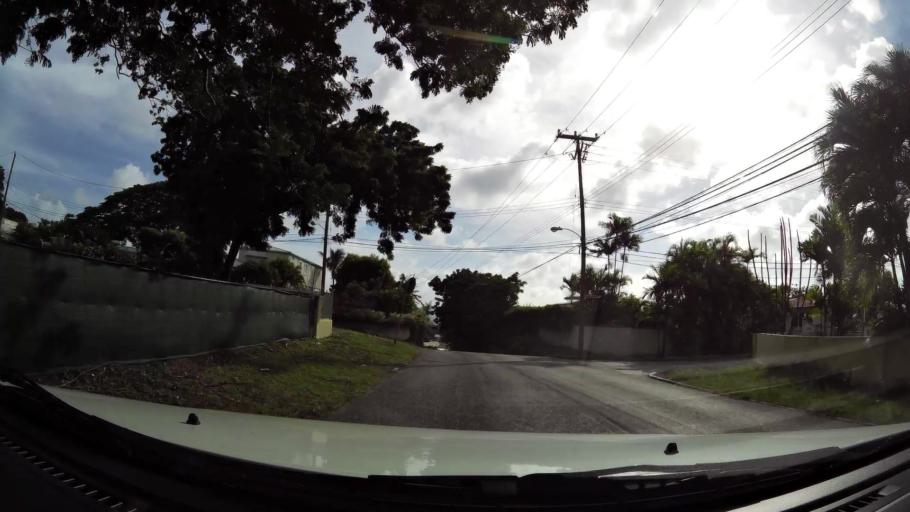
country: BB
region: Saint Michael
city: Bridgetown
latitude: 13.0811
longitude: -59.5794
